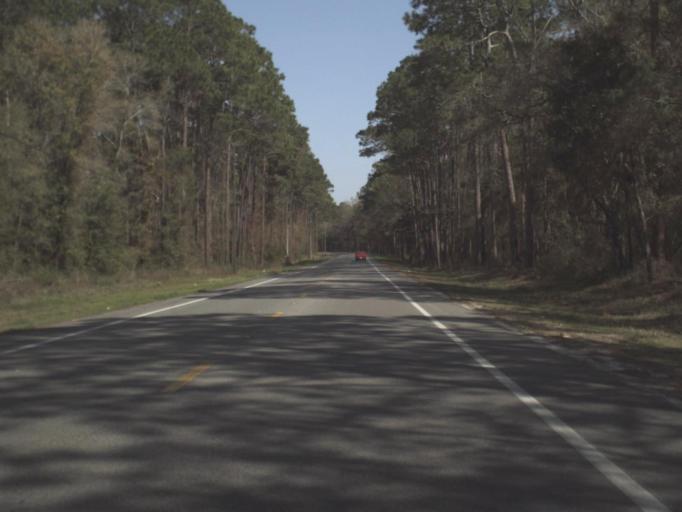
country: US
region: Florida
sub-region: Wakulla County
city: Crawfordville
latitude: 30.0765
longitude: -84.4123
